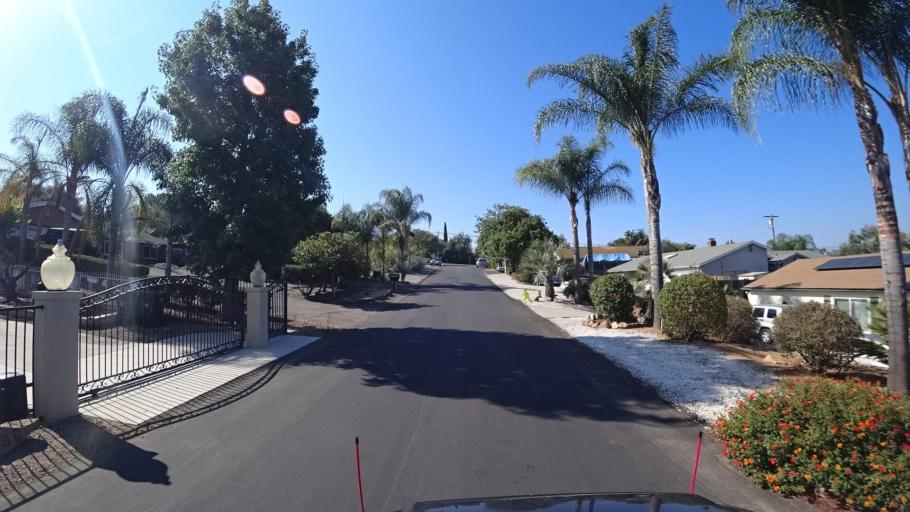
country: US
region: California
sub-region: San Diego County
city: Fallbrook
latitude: 33.3921
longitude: -117.2348
